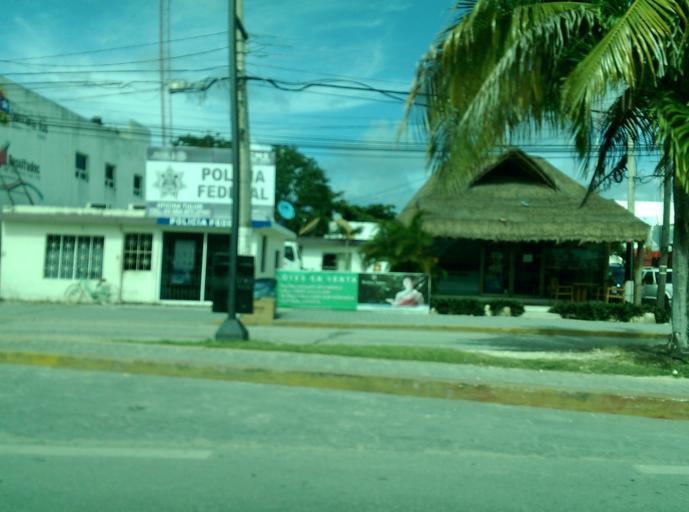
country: MX
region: Quintana Roo
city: Tulum
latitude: 20.2122
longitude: -87.4595
